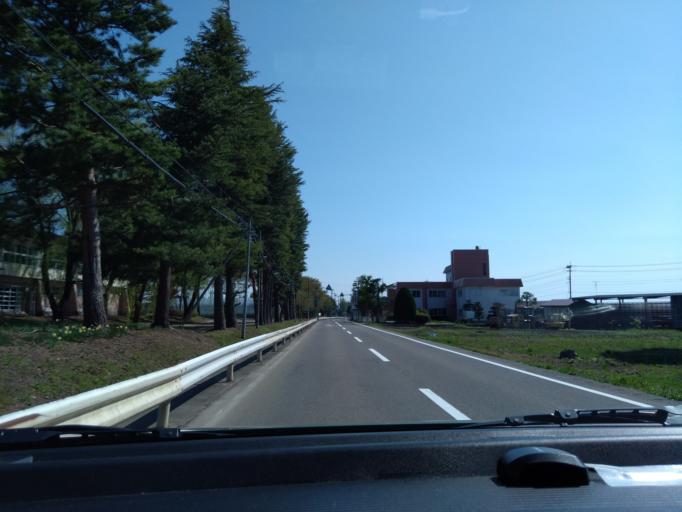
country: JP
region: Akita
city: Omagari
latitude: 39.4656
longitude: 140.5821
